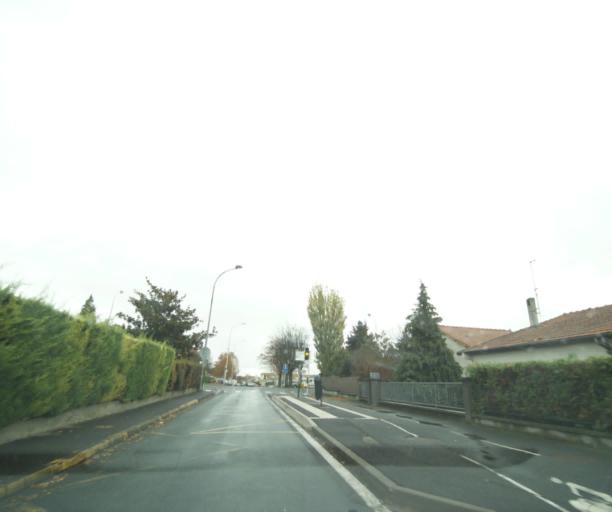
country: FR
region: Auvergne
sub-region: Departement du Puy-de-Dome
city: Cournon-d'Auvergne
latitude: 45.7310
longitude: 3.1992
